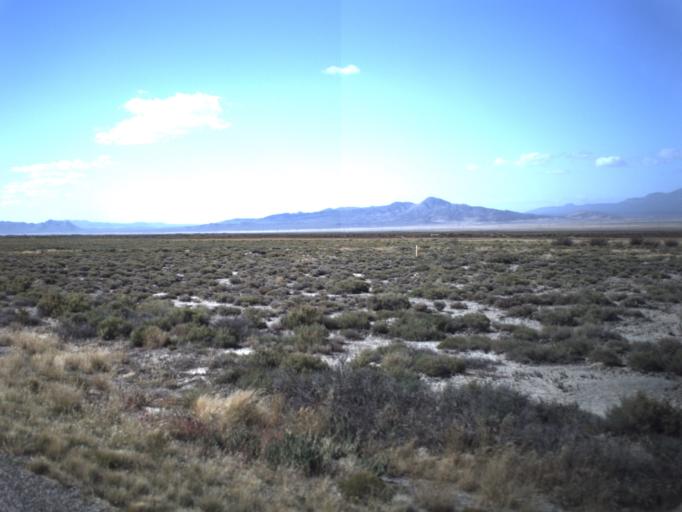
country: US
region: Utah
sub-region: Beaver County
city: Milford
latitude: 38.6373
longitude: -112.9836
